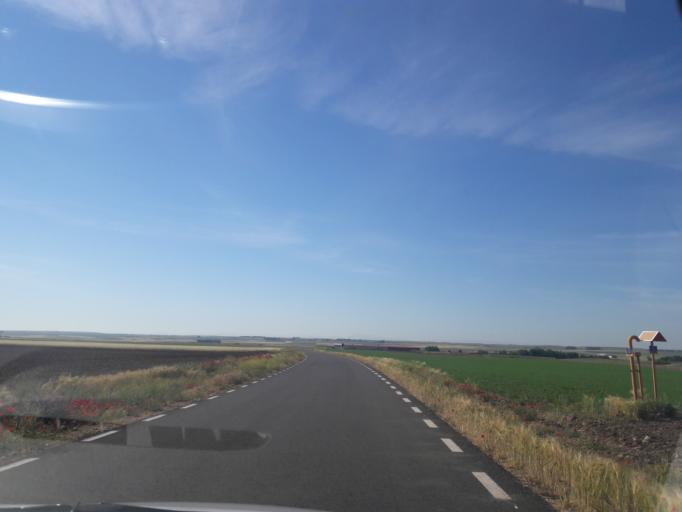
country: ES
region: Castille and Leon
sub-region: Provincia de Salamanca
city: Espino de la Orbada
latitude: 41.1206
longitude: -5.4284
